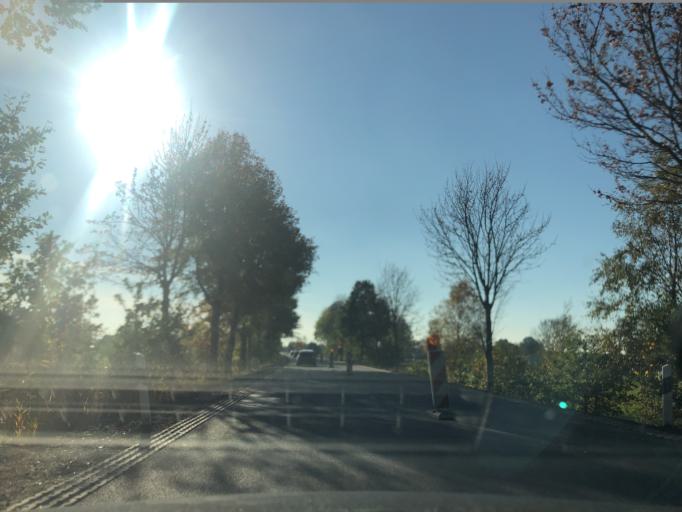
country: DE
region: Lower Saxony
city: Lemwerder
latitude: 53.1514
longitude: 8.5508
